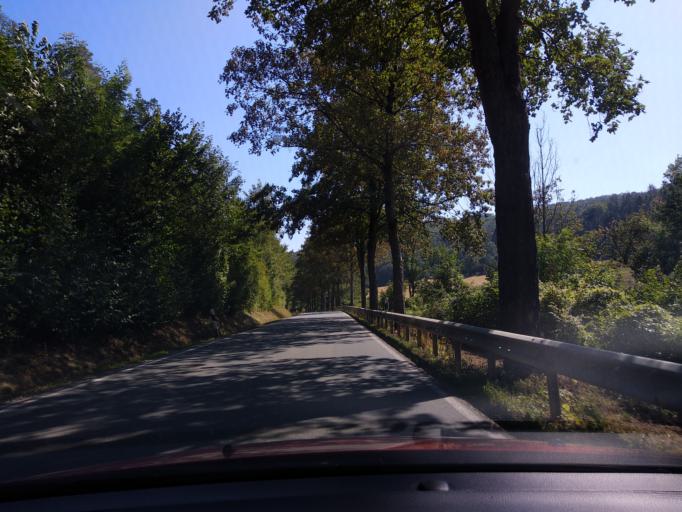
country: DE
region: North Rhine-Westphalia
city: Beverungen
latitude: 51.6770
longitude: 9.3543
